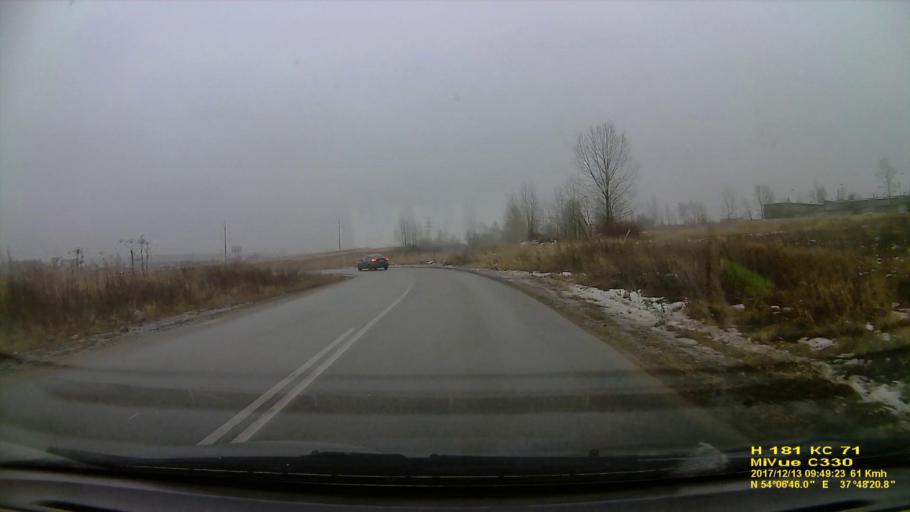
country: RU
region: Tula
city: Bolokhovo
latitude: 54.1127
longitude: 37.8061
